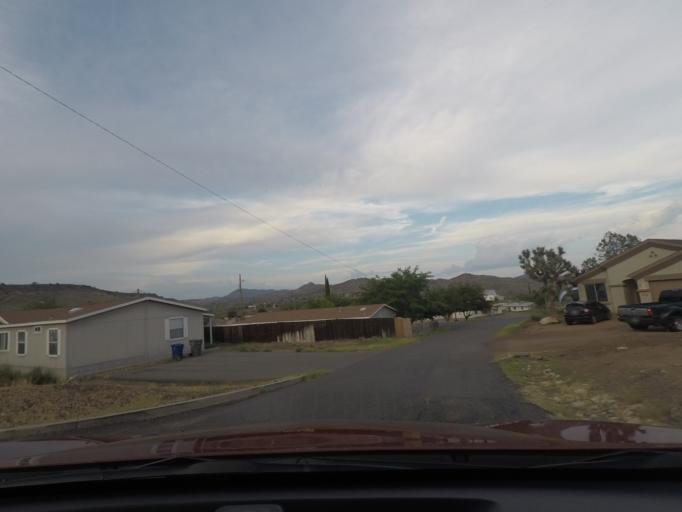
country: US
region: Arizona
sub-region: Yavapai County
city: Bagdad
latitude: 34.5731
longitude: -113.1850
